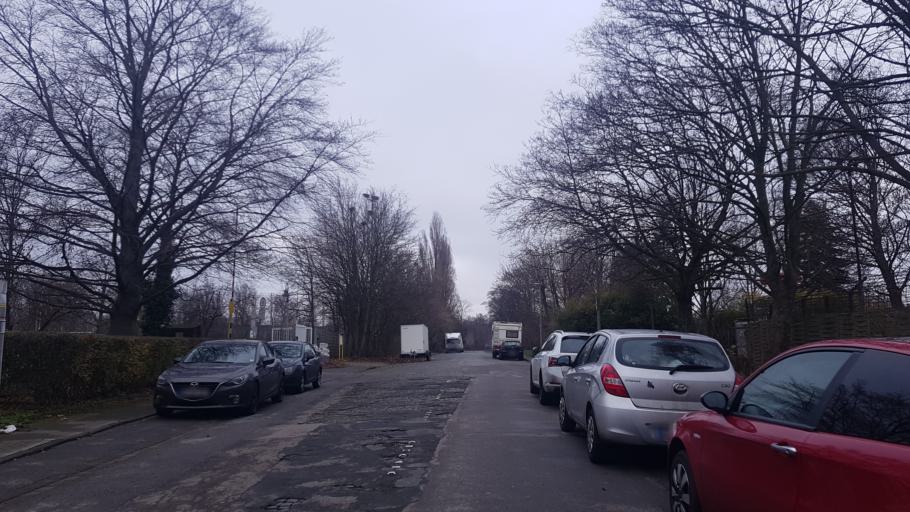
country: DE
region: North Rhine-Westphalia
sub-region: Regierungsbezirk Dusseldorf
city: Duisburg
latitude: 51.4437
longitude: 6.7819
